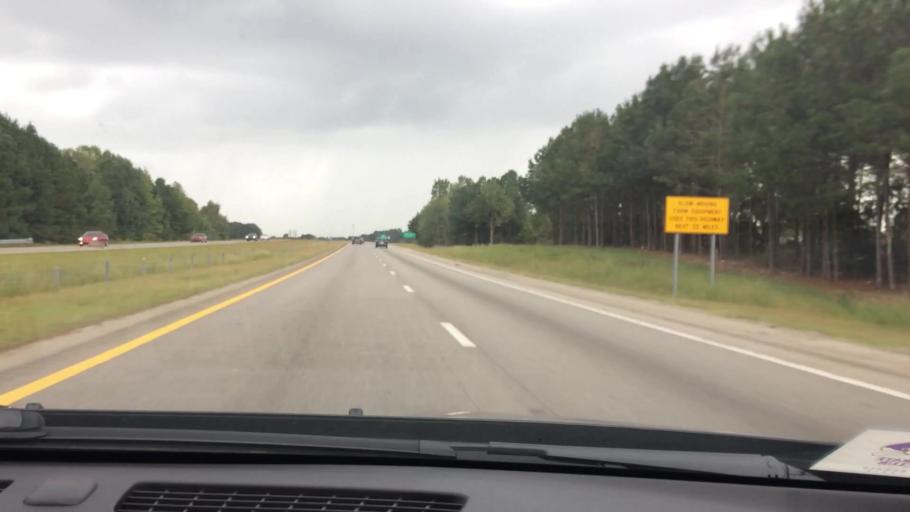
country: US
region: North Carolina
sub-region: Wilson County
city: Lucama
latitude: 35.7266
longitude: -78.0081
